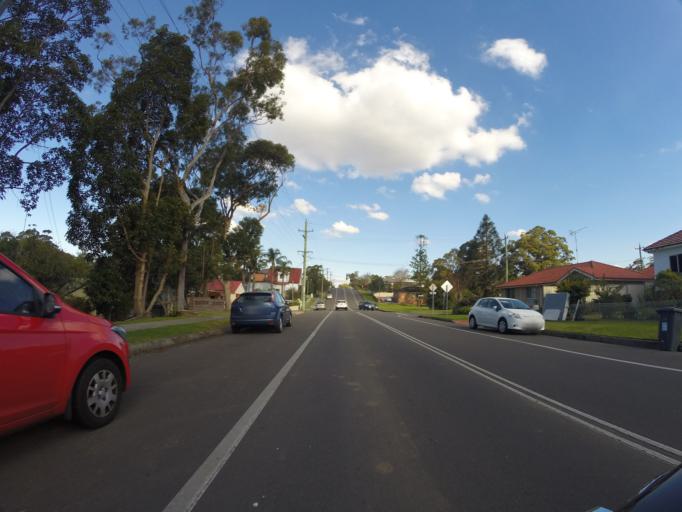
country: AU
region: New South Wales
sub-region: Wollongong
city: Keiraville
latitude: -34.4121
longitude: 150.8709
